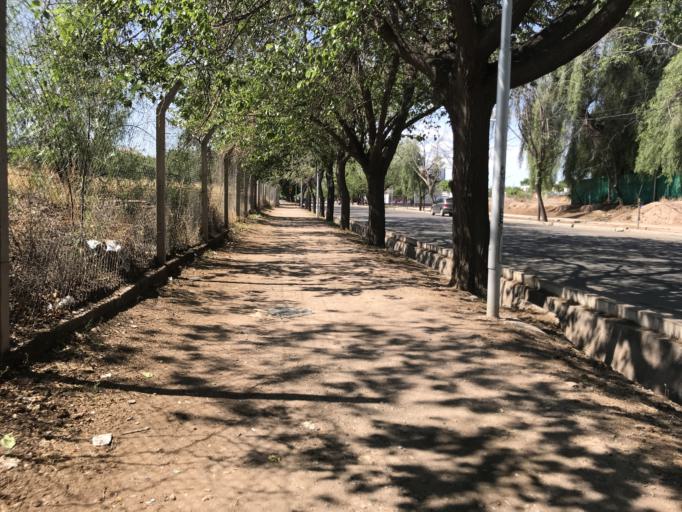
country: AR
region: Mendoza
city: Mendoza
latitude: -32.8796
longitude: -68.8392
